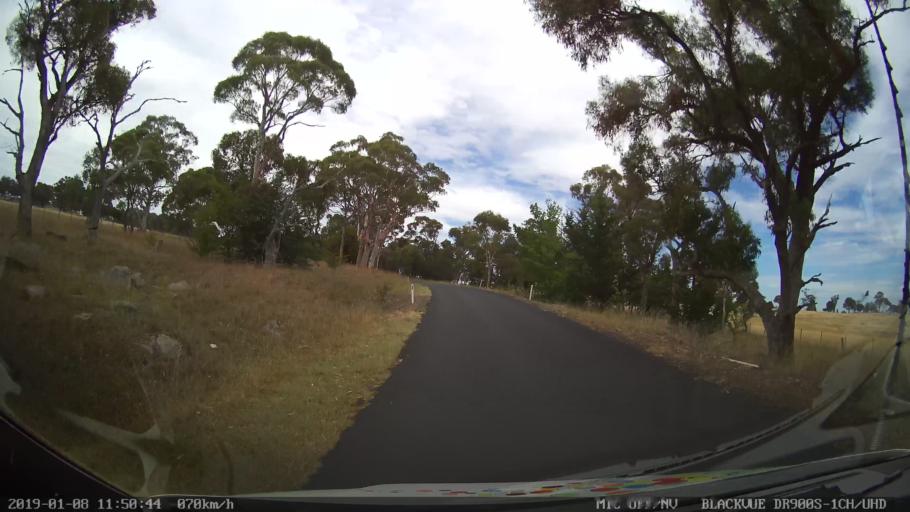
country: AU
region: New South Wales
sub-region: Armidale Dumaresq
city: Armidale
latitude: -30.3858
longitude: 151.5575
